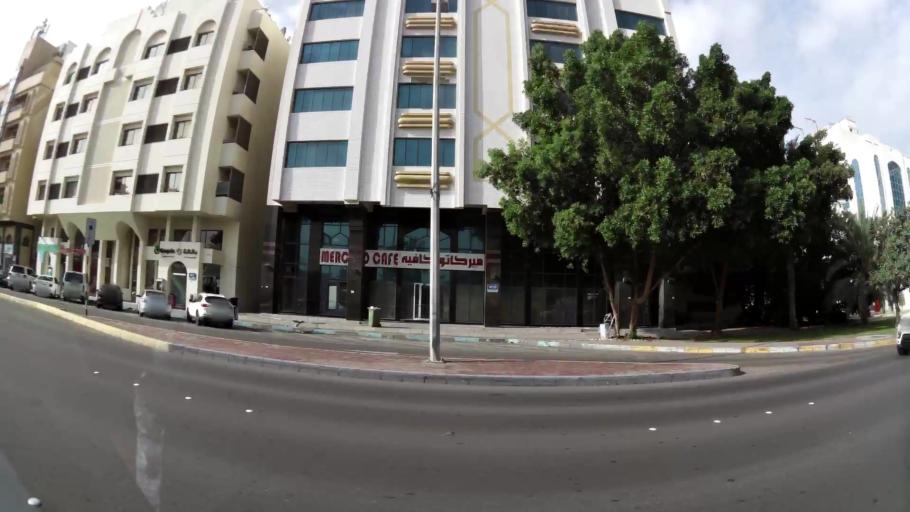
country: AE
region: Abu Dhabi
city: Abu Dhabi
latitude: 24.4566
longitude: 54.3913
